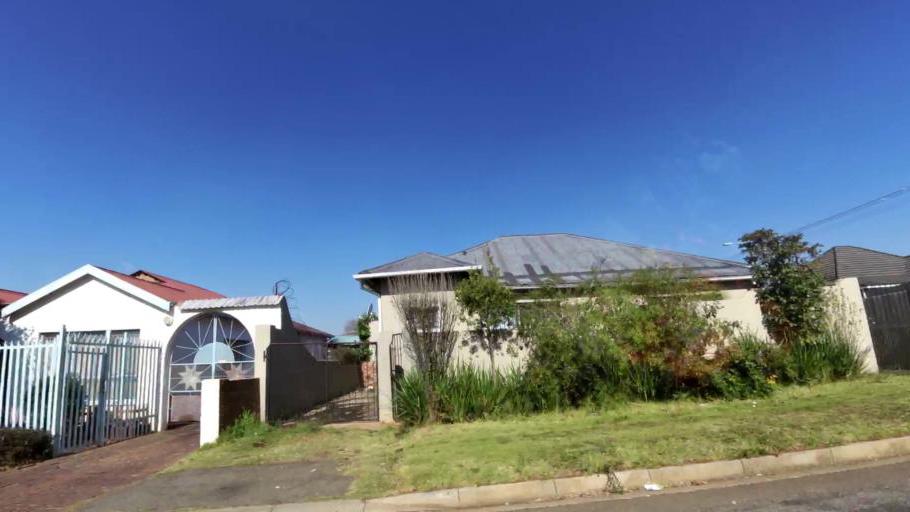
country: ZA
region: Gauteng
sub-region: City of Johannesburg Metropolitan Municipality
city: Johannesburg
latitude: -26.1702
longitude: 27.9661
